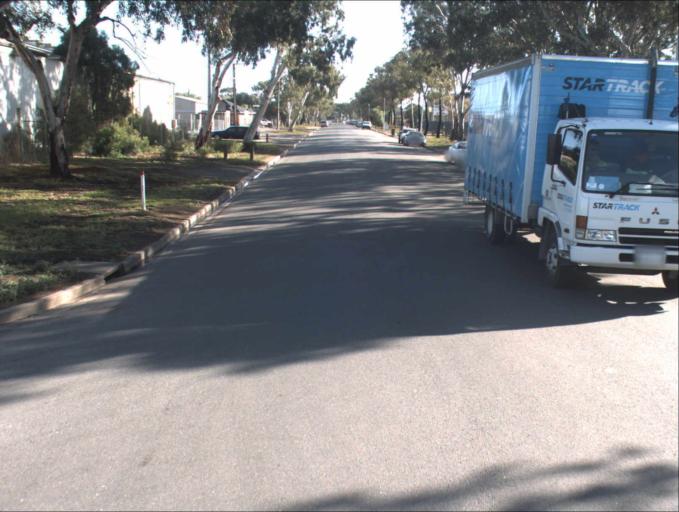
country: AU
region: South Australia
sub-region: Charles Sturt
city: Woodville North
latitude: -34.8435
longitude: 138.5523
